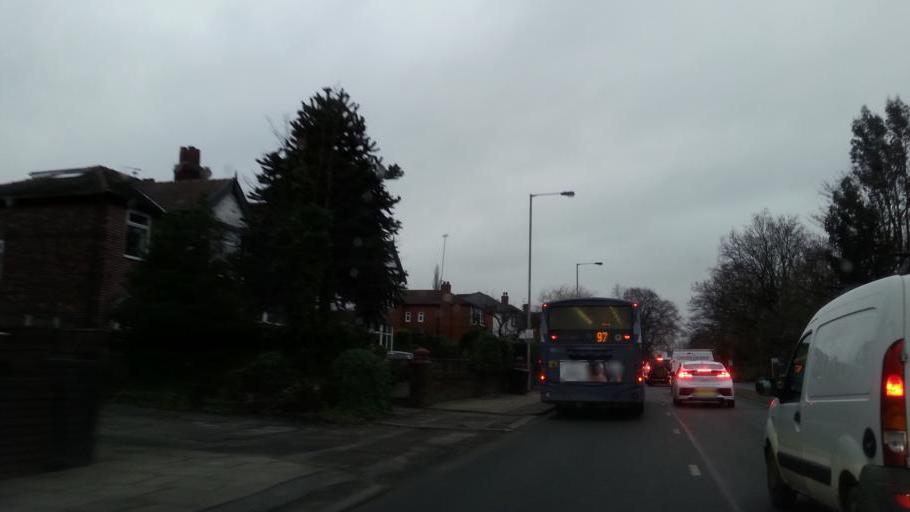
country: GB
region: England
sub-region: Borough of Bury
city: Prestwich
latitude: 53.5242
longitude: -2.2771
